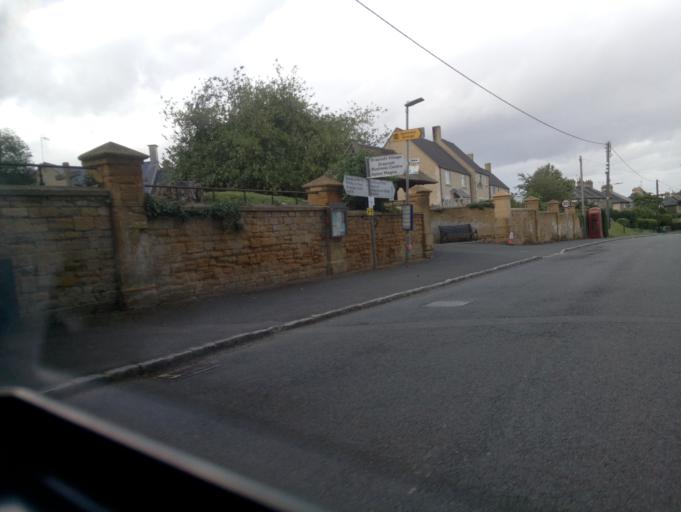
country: GB
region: England
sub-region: Gloucestershire
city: Chipping Campden
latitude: 52.0155
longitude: -1.7576
